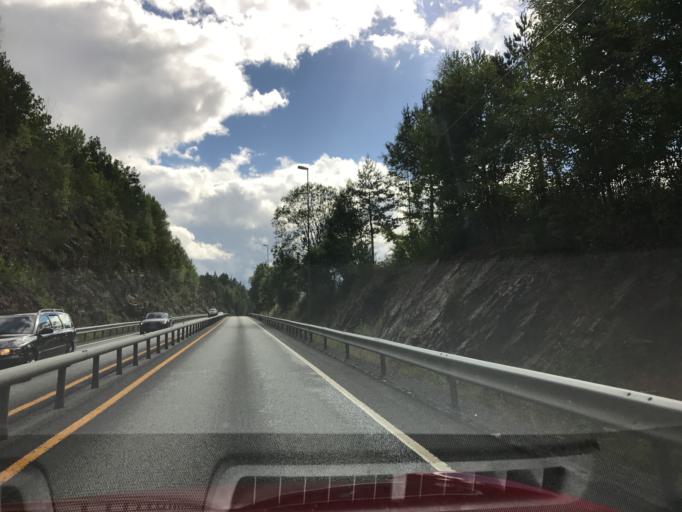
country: NO
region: Aust-Agder
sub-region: Gjerstad
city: Gjerstad
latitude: 58.8427
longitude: 9.1035
